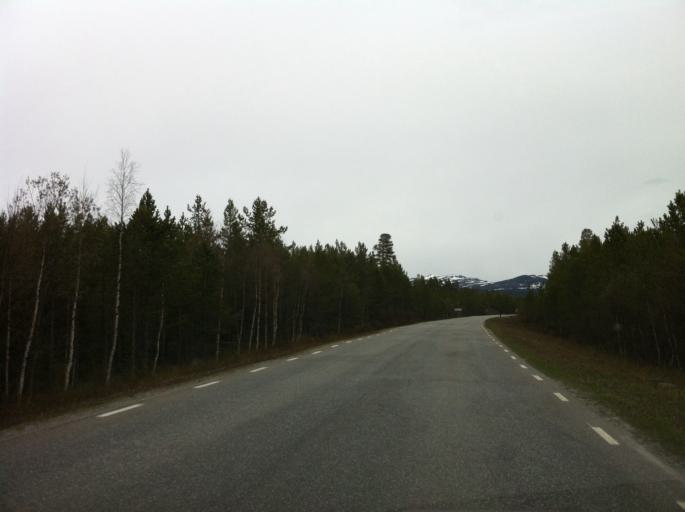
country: NO
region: Hedmark
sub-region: Engerdal
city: Engerdal
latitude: 62.5258
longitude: 12.5814
